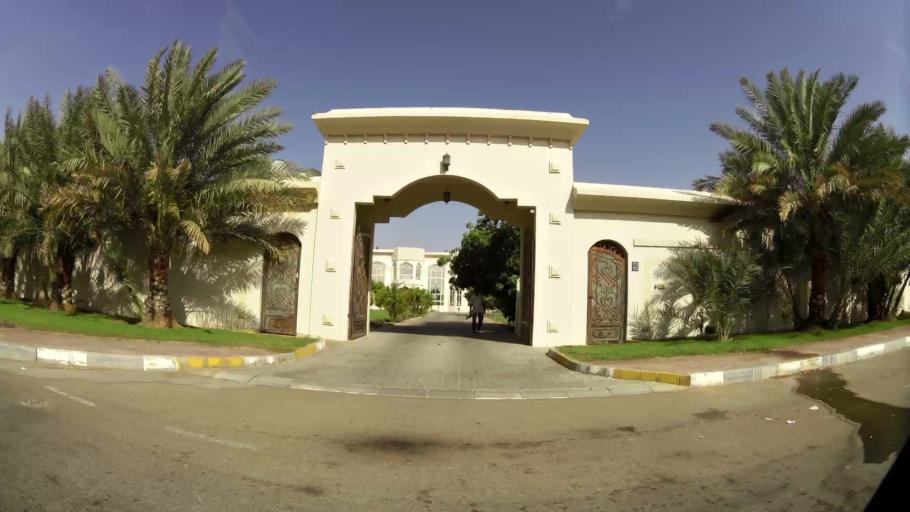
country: OM
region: Al Buraimi
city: Al Buraymi
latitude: 24.3372
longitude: 55.7913
